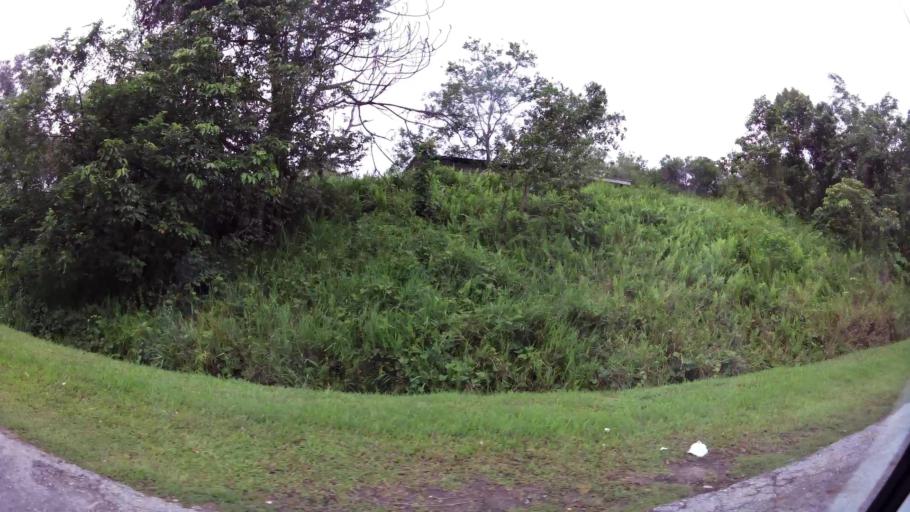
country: BN
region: Brunei and Muara
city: Bandar Seri Begawan
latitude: 4.8832
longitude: 114.9136
